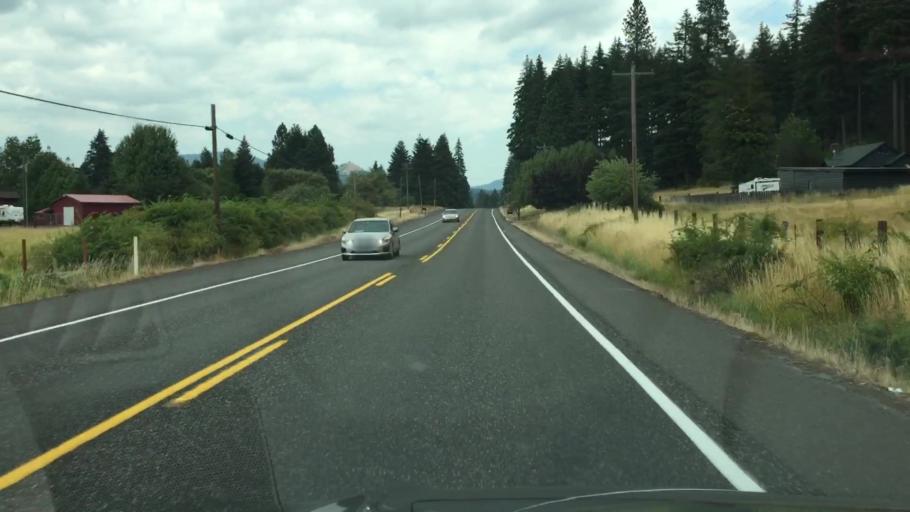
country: US
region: Washington
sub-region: Klickitat County
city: White Salmon
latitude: 45.7848
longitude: -121.5025
